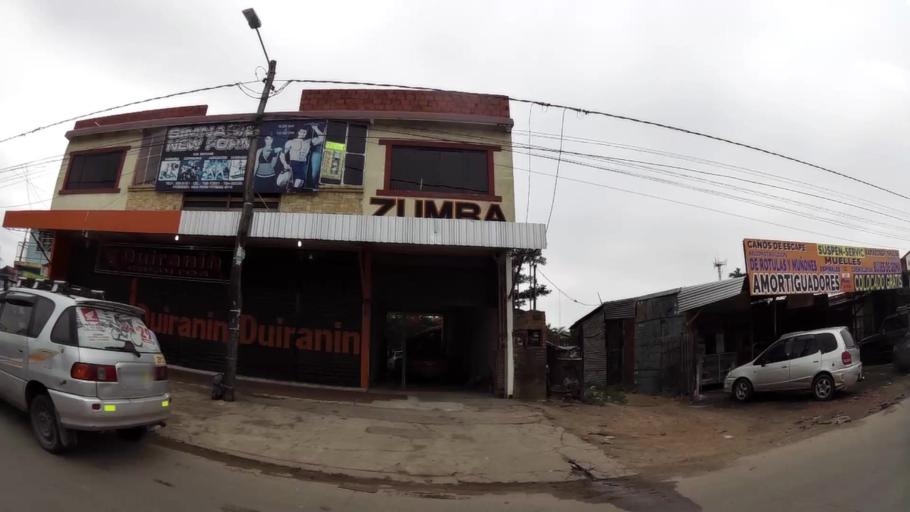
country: BO
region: Santa Cruz
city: Santa Cruz de la Sierra
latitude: -17.8259
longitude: -63.1680
